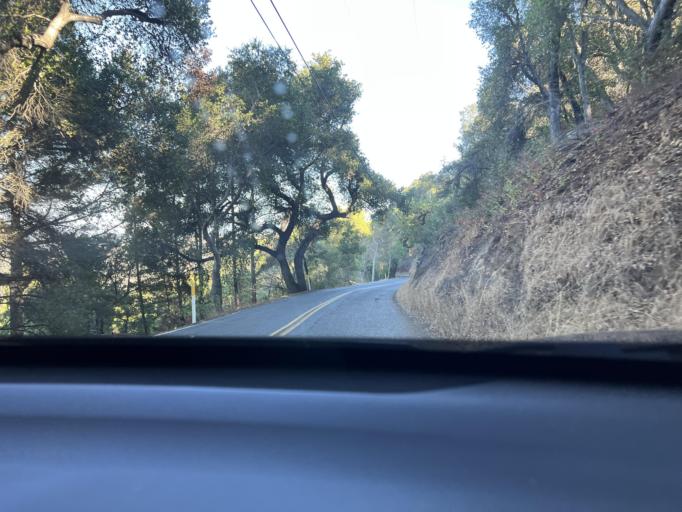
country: US
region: California
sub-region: Santa Clara County
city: Loyola
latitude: 37.2878
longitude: -122.0910
